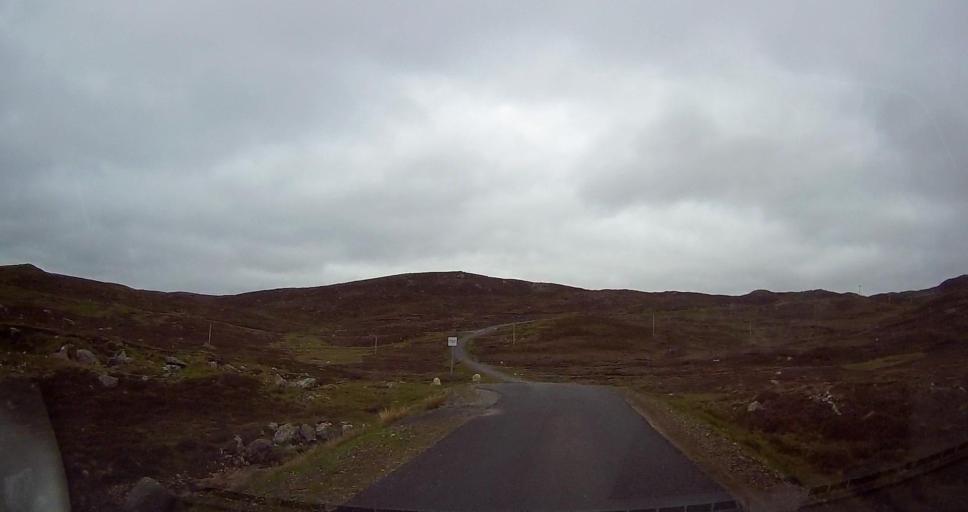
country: GB
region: Scotland
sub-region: Shetland Islands
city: Lerwick
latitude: 60.3379
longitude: -1.3194
